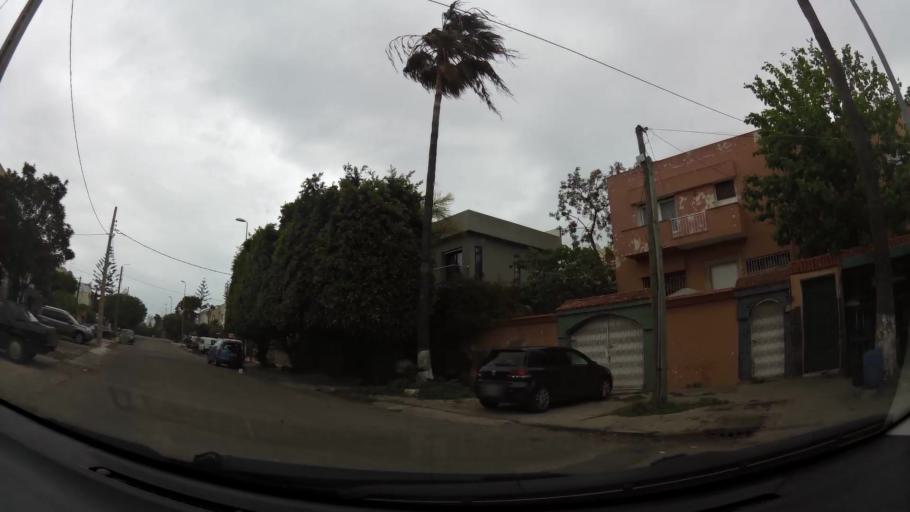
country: MA
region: Grand Casablanca
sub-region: Casablanca
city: Casablanca
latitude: 33.5750
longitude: -7.6665
